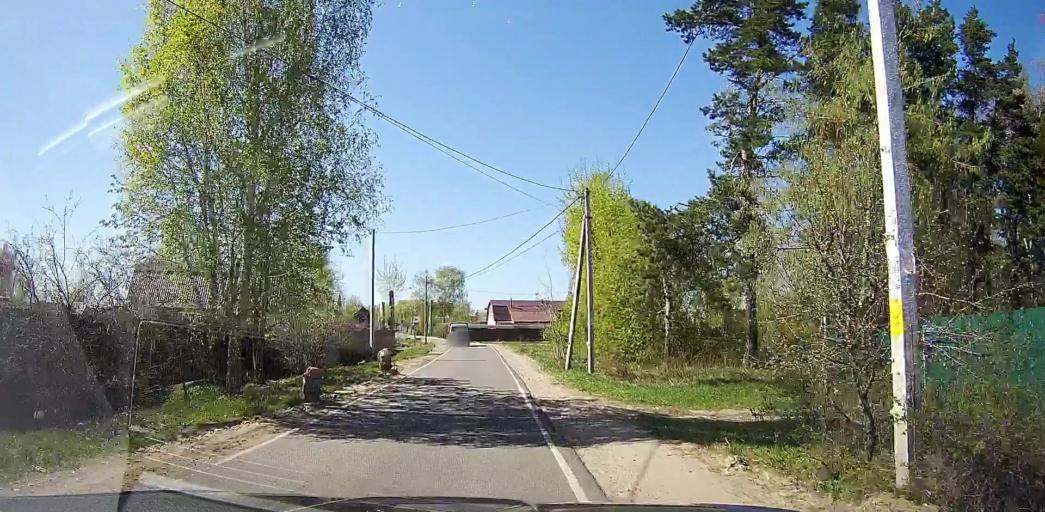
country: RU
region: Moskovskaya
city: Malyshevo
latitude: 55.4628
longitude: 38.3583
